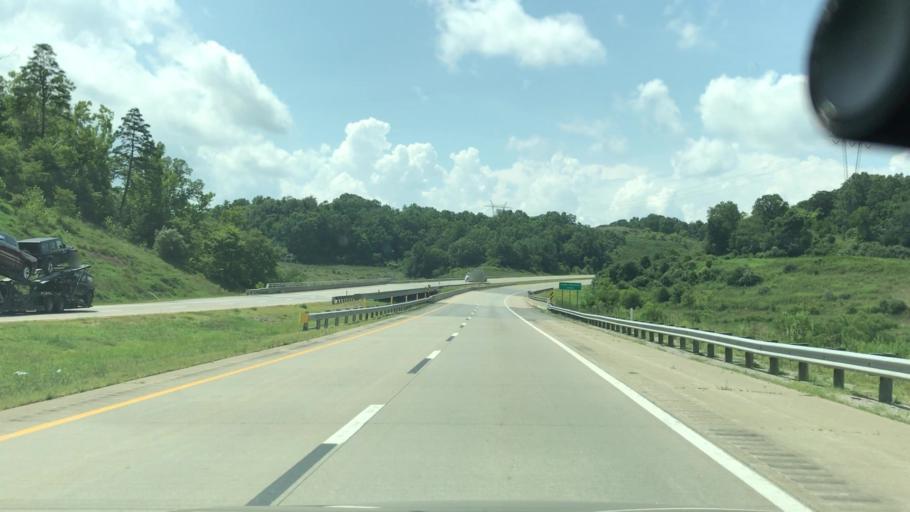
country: US
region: West Virginia
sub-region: Mason County
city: Point Pleasant
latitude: 38.7713
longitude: -82.0468
